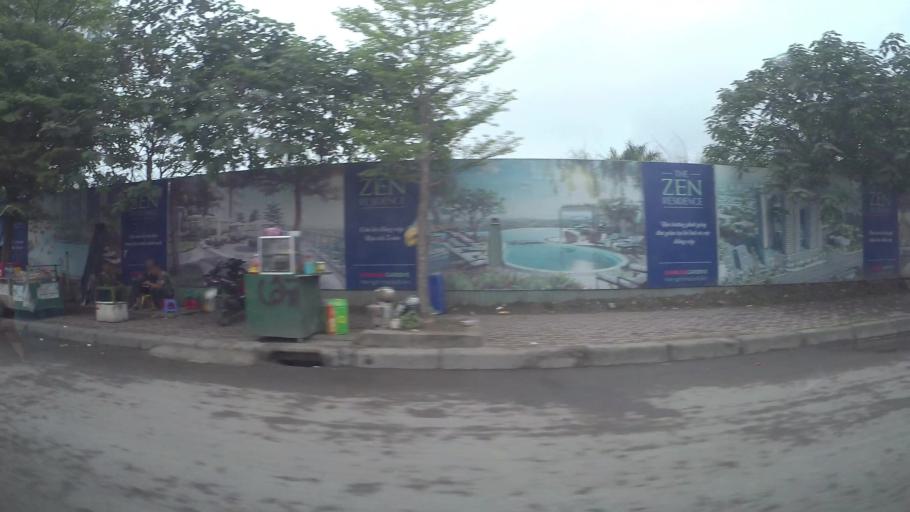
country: VN
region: Ha Noi
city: Van Dien
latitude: 20.9724
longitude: 105.8807
